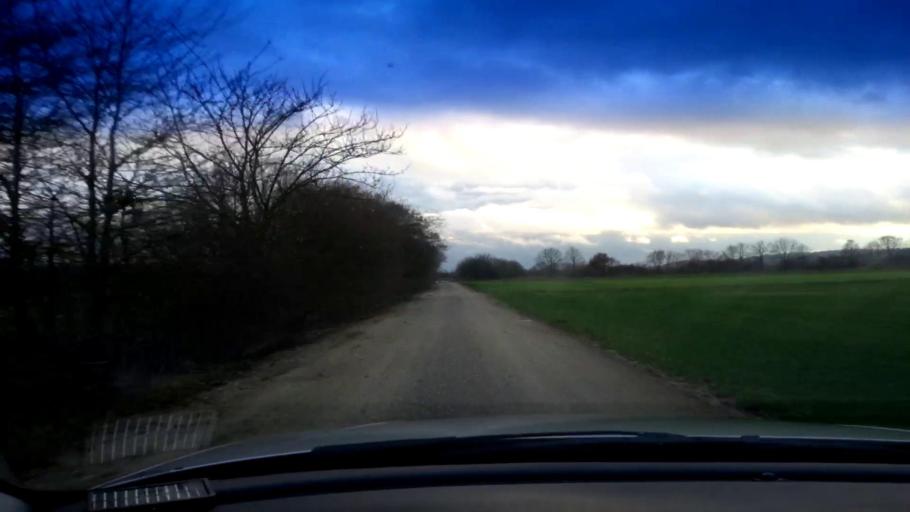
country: DE
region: Bavaria
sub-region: Upper Franconia
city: Rattelsdorf
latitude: 50.0041
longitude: 10.8947
